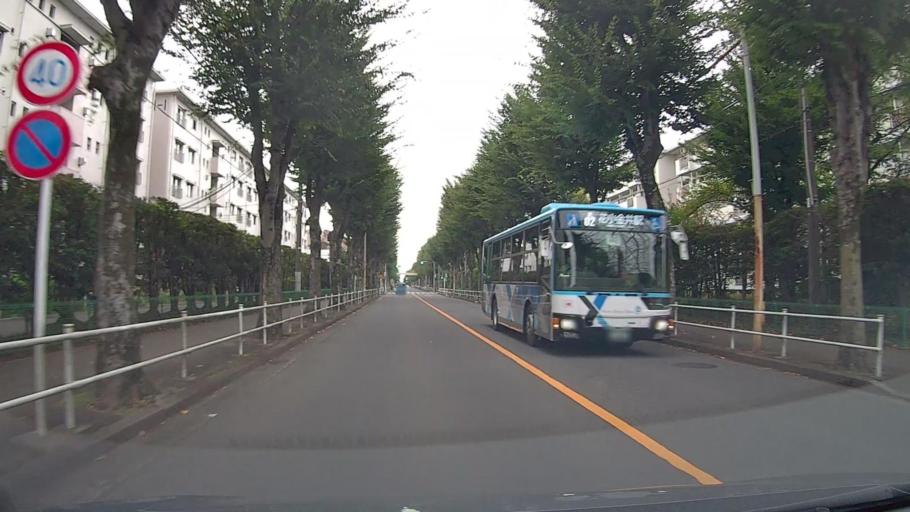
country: JP
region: Tokyo
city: Tanashicho
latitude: 35.7443
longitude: 139.5076
